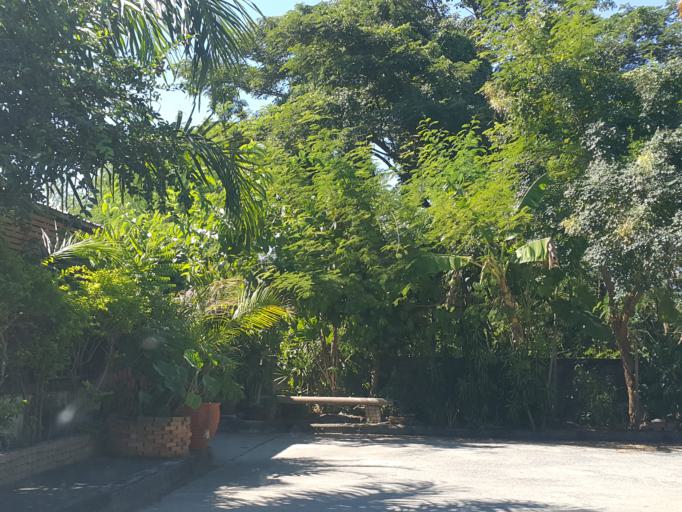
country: TH
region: Chiang Mai
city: San Sai
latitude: 18.8333
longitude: 99.0545
